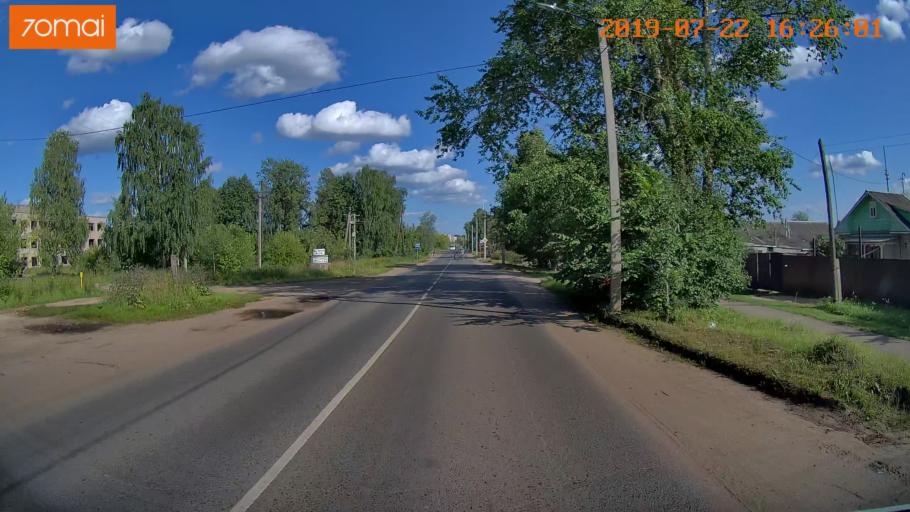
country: RU
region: Ivanovo
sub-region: Gorod Ivanovo
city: Ivanovo
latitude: 57.0510
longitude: 40.9293
